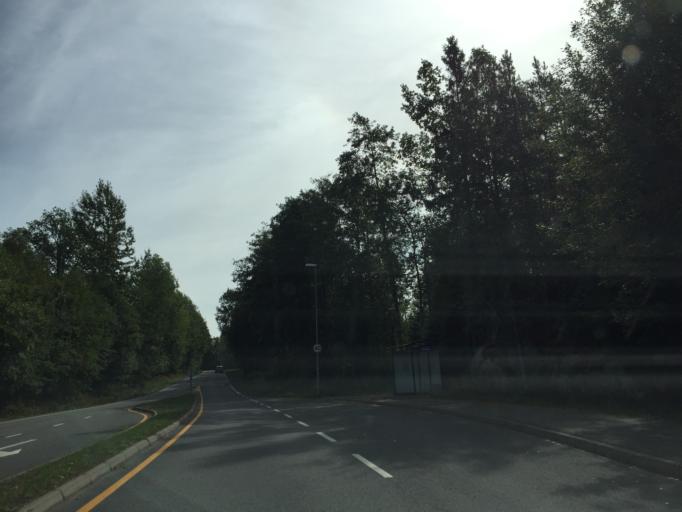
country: NO
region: Ostfold
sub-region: Moss
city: Moss
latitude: 59.4883
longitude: 10.6926
